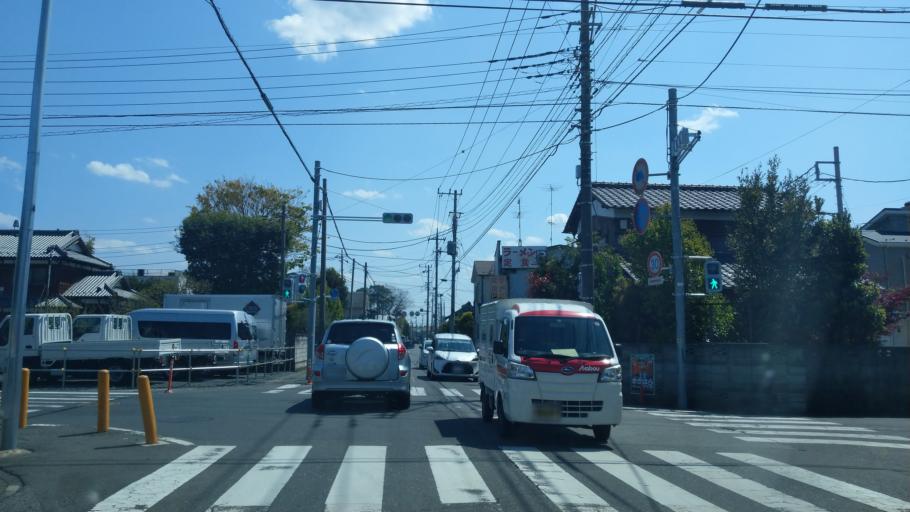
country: JP
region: Saitama
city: Yono
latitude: 35.8882
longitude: 139.6110
